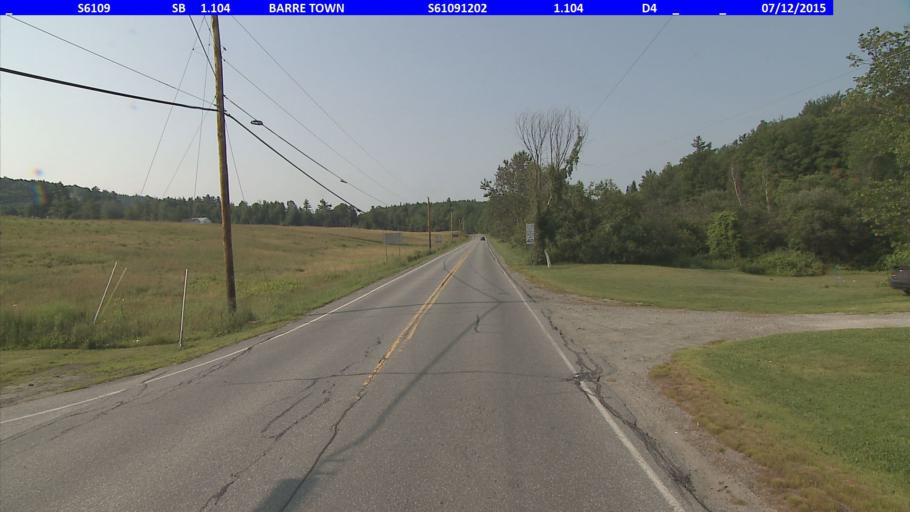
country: US
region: Vermont
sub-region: Washington County
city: South Barre
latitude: 44.1701
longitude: -72.4917
